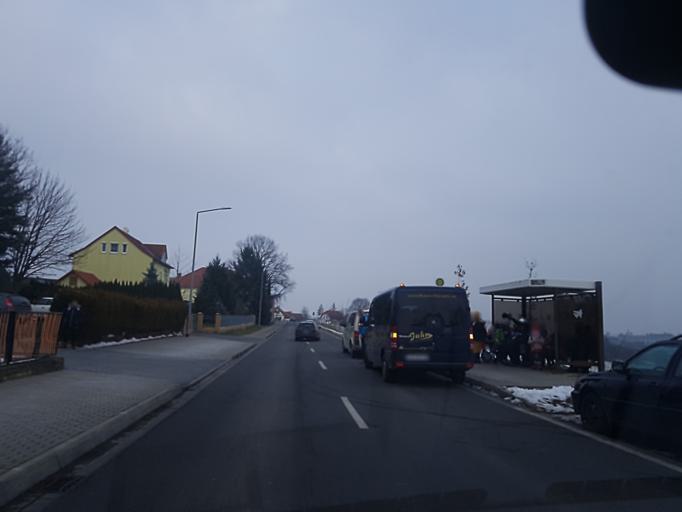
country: DE
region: Saxony
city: Mugeln
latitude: 51.2213
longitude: 13.0031
